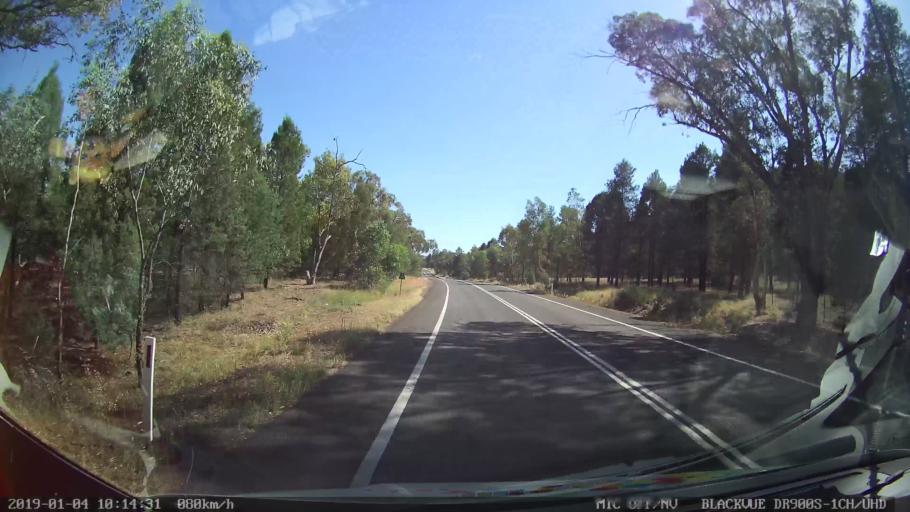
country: AU
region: New South Wales
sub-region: Cabonne
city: Canowindra
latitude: -33.3962
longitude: 148.4143
